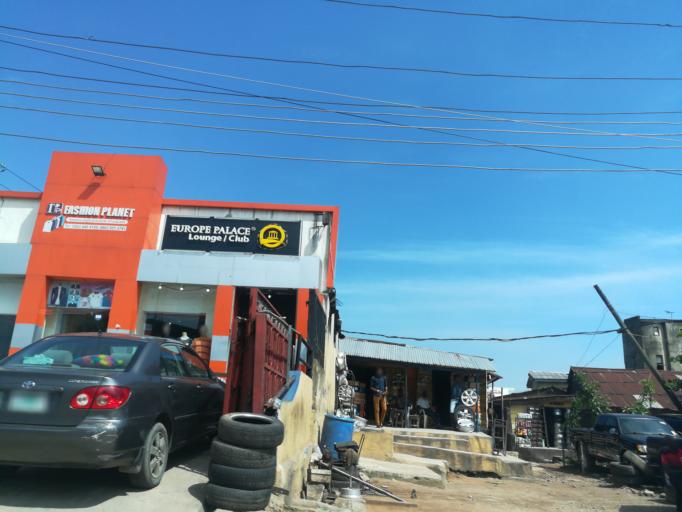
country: NG
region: Lagos
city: Ikeja
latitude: 6.6064
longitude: 3.3481
